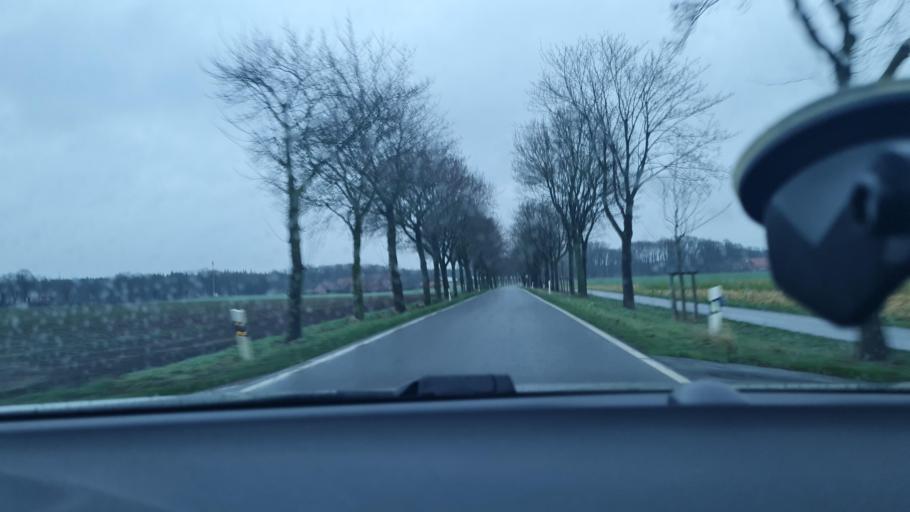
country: DE
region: North Rhine-Westphalia
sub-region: Regierungsbezirk Munster
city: Heiden
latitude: 51.7698
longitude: 6.9258
